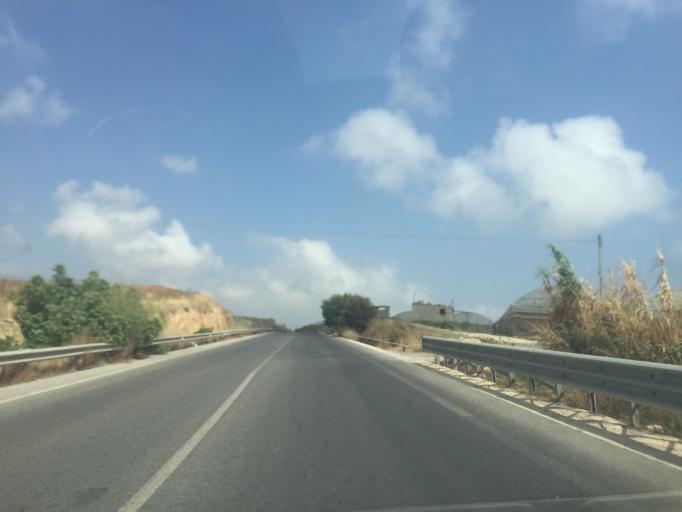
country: IT
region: Sicily
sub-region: Ragusa
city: Donnalucata
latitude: 36.7732
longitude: 14.6203
